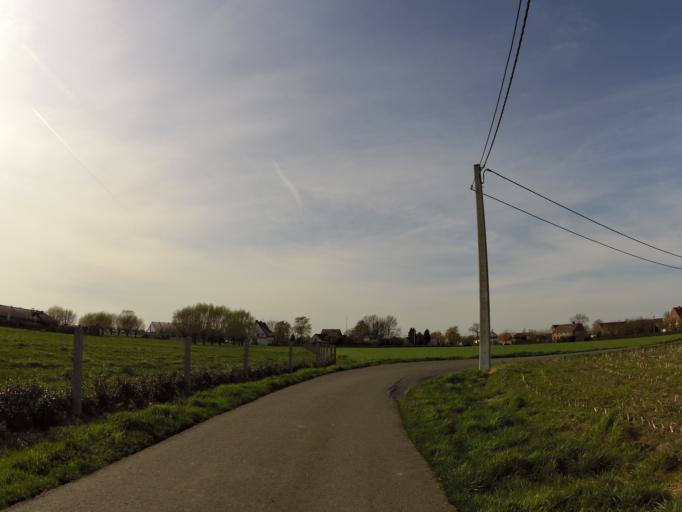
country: BE
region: Flanders
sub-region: Provincie West-Vlaanderen
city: Ichtegem
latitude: 51.1436
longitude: 3.0361
